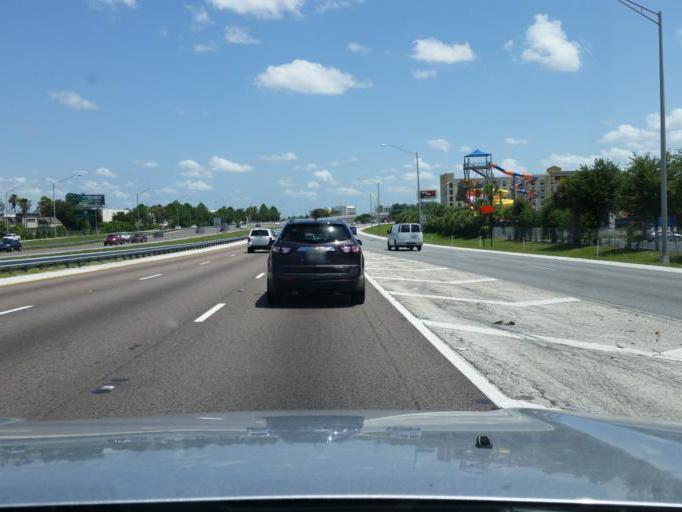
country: US
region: Florida
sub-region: Orange County
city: Doctor Phillips
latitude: 28.4526
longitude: -81.4741
